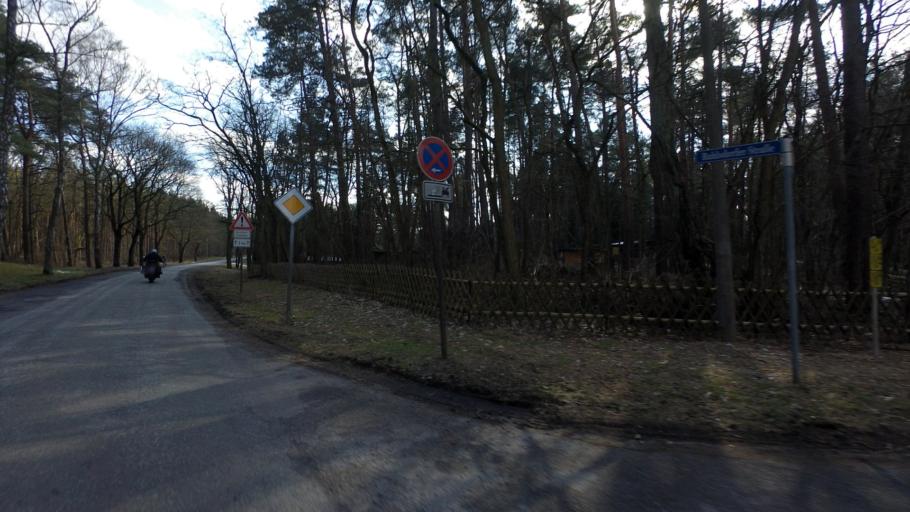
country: DE
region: Brandenburg
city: Biesenthal
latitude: 52.7787
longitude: 13.6144
